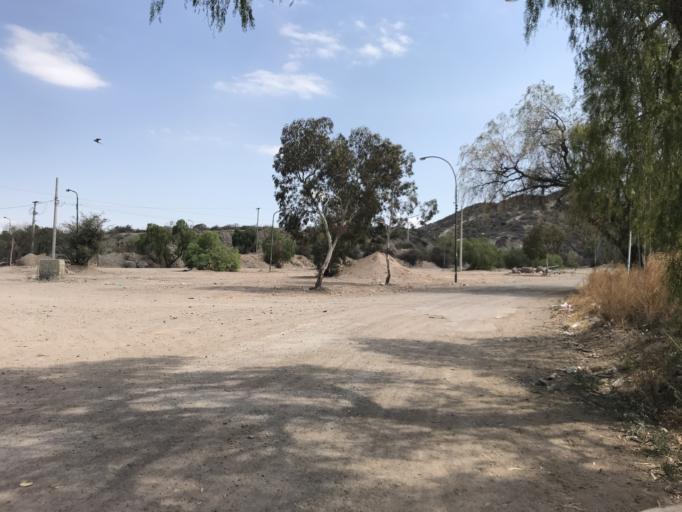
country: AR
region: Mendoza
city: Mendoza
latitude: -32.8901
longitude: -68.8857
